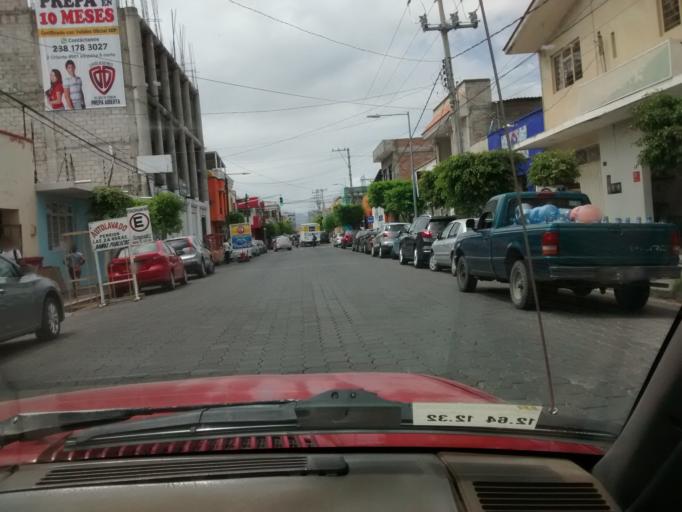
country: MX
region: Puebla
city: Tehuacan
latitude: 18.4639
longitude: -97.3981
